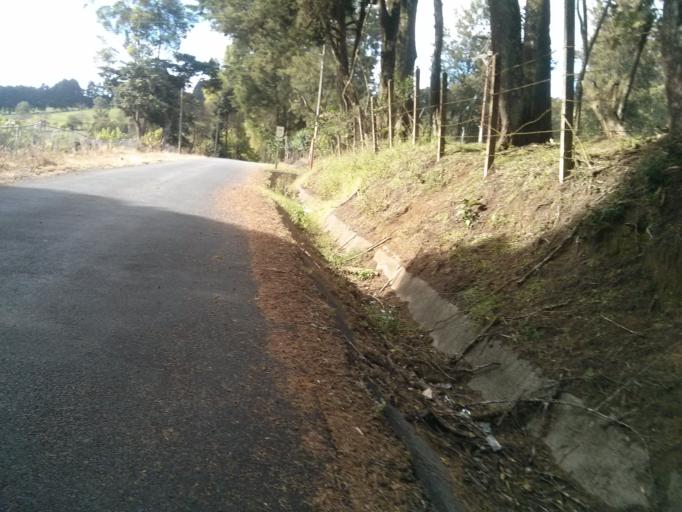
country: CR
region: Cartago
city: Tres Rios
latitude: 9.9142
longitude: -83.9521
